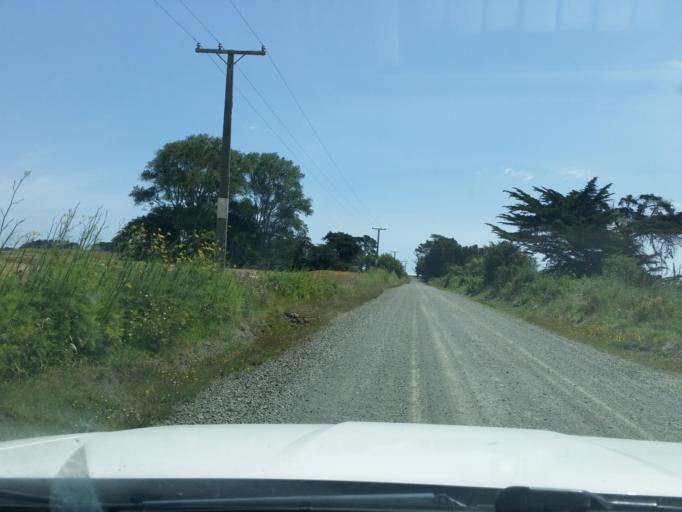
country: NZ
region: Northland
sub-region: Kaipara District
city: Dargaville
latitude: -35.9063
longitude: 173.8074
